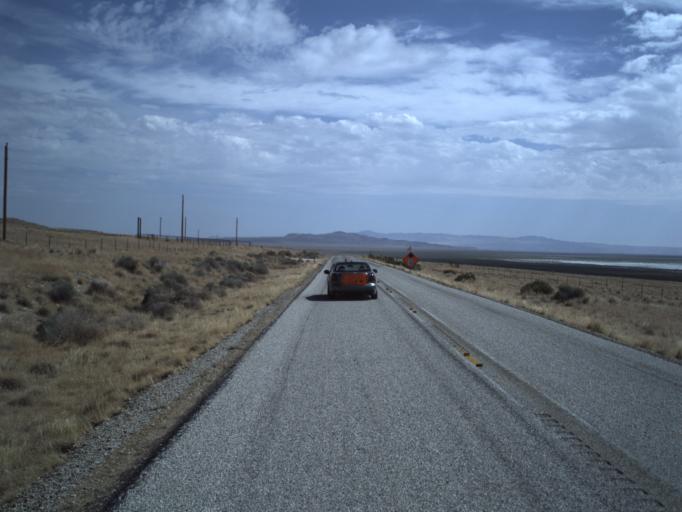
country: US
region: Utah
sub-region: Tooele County
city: Wendover
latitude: 41.4404
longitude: -113.7097
